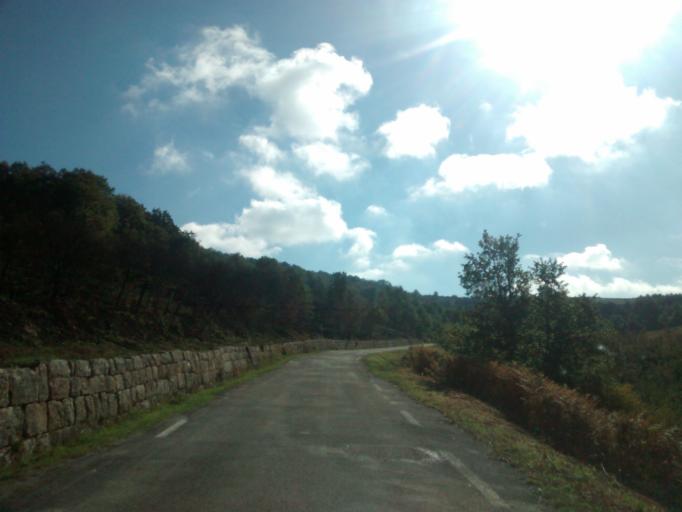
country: ES
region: Castille and Leon
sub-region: Provincia de Burgos
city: Arija
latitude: 42.9314
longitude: -4.0146
